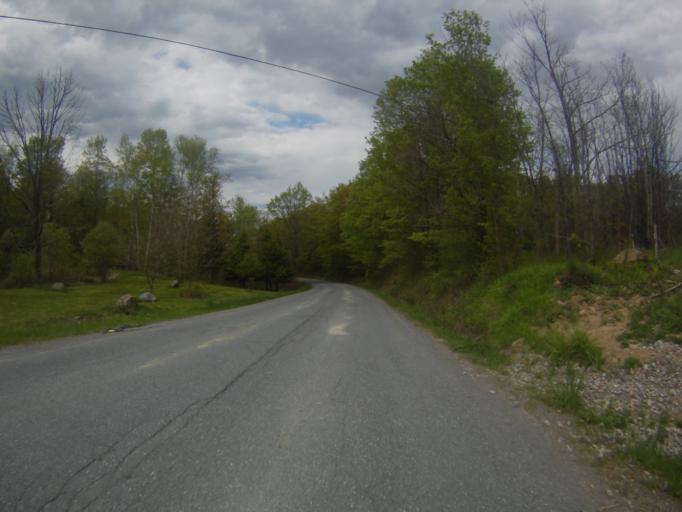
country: US
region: New York
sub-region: Essex County
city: Ticonderoga
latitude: 43.9252
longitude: -73.5036
